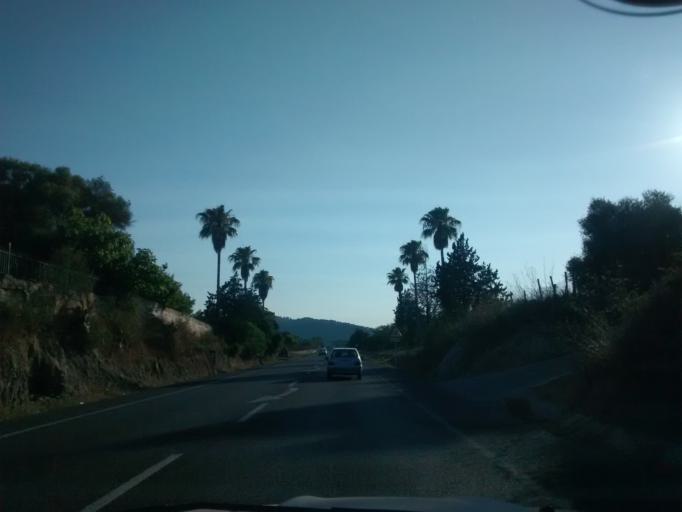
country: ES
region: Balearic Islands
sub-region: Illes Balears
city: Alcudia
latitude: 39.8439
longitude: 3.0896
